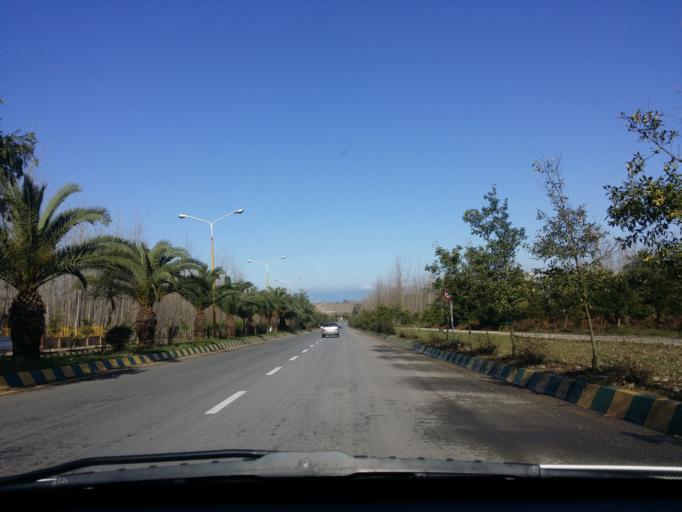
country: IR
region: Mazandaran
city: Chalus
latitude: 36.6684
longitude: 51.3072
